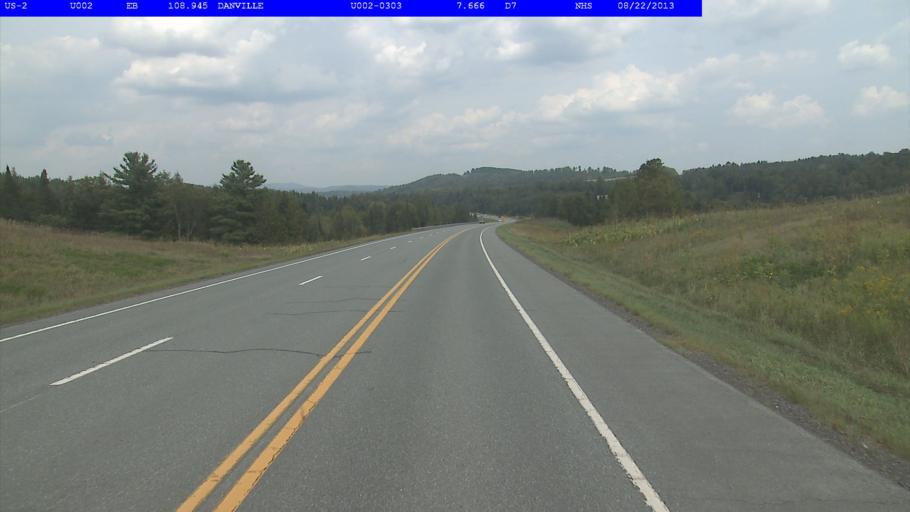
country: US
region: Vermont
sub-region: Caledonia County
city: St Johnsbury
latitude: 44.4340
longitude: -72.0847
